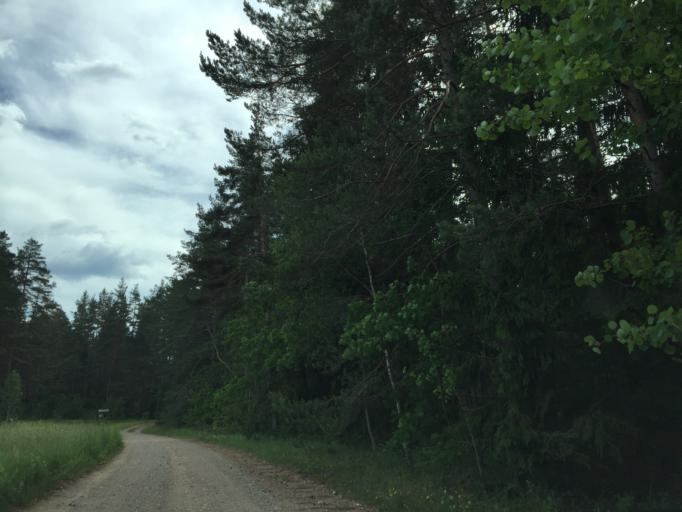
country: LV
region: Engure
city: Smarde
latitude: 57.0507
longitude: 23.2891
